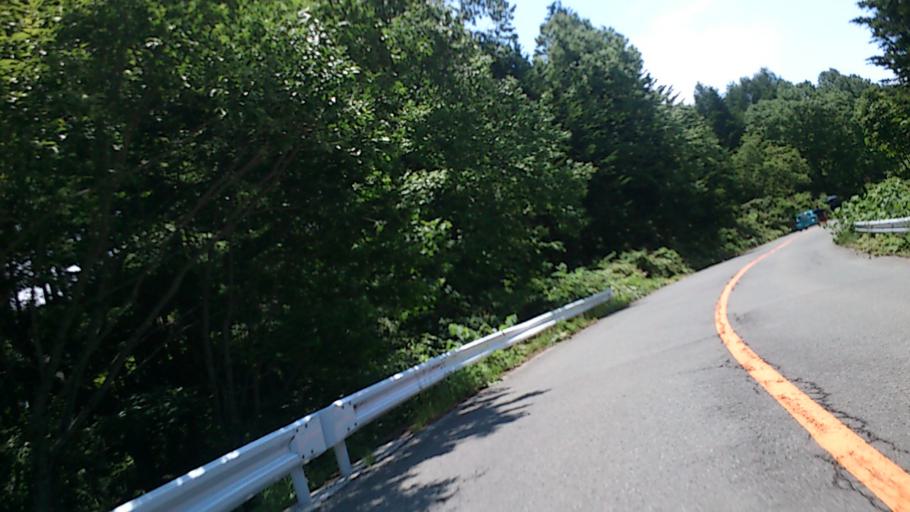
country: JP
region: Yamagata
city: Yamagata-shi
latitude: 38.1235
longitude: 140.4040
